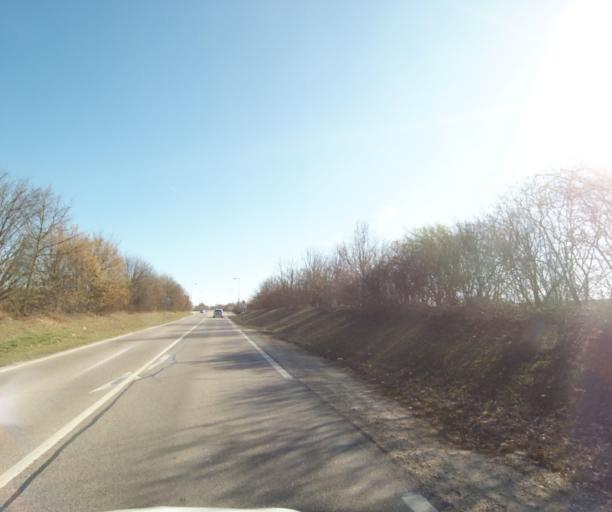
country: FR
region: Lorraine
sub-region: Departement de Meurthe-et-Moselle
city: Tomblaine
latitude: 48.6819
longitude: 6.2228
